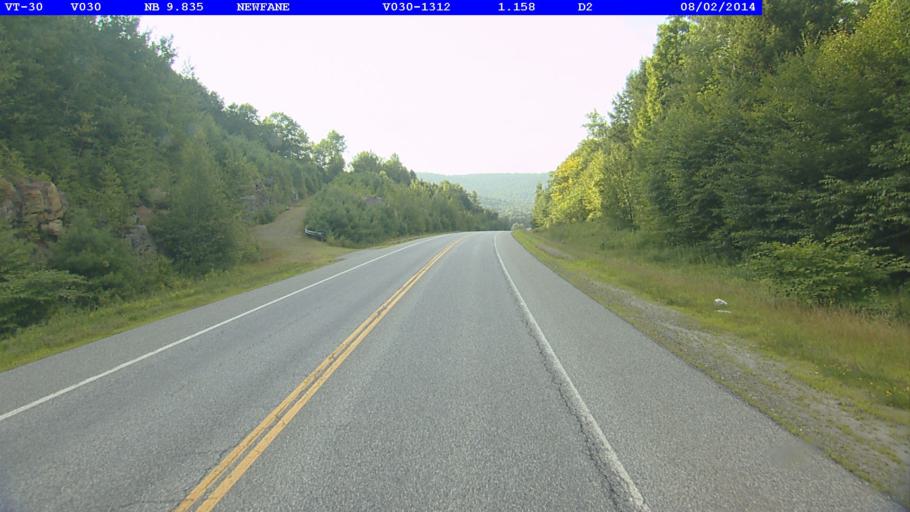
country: US
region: Vermont
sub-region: Windham County
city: Newfane
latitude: 42.9616
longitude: -72.6528
